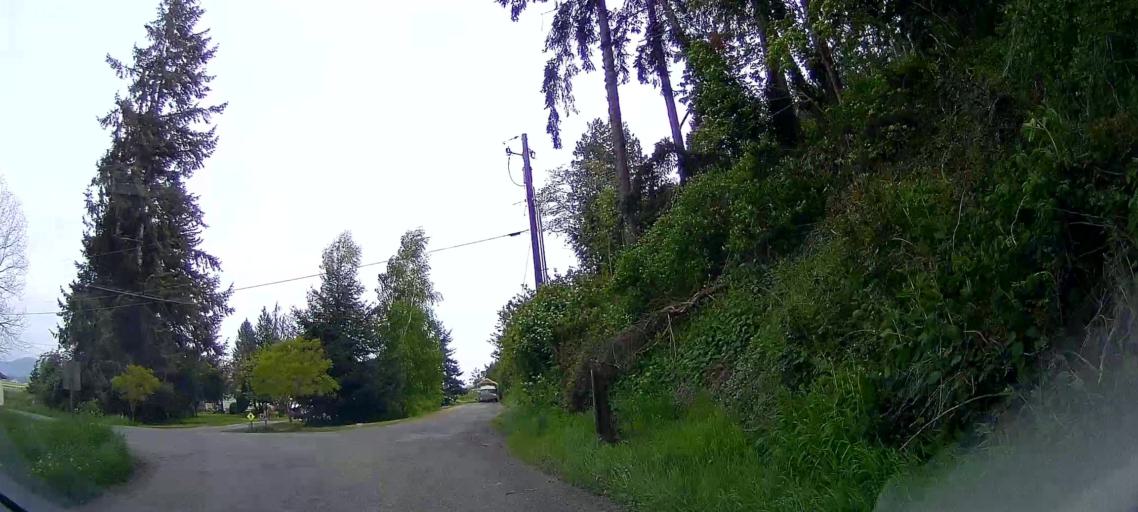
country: US
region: Washington
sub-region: Skagit County
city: Mount Vernon
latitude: 48.3943
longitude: -122.4448
